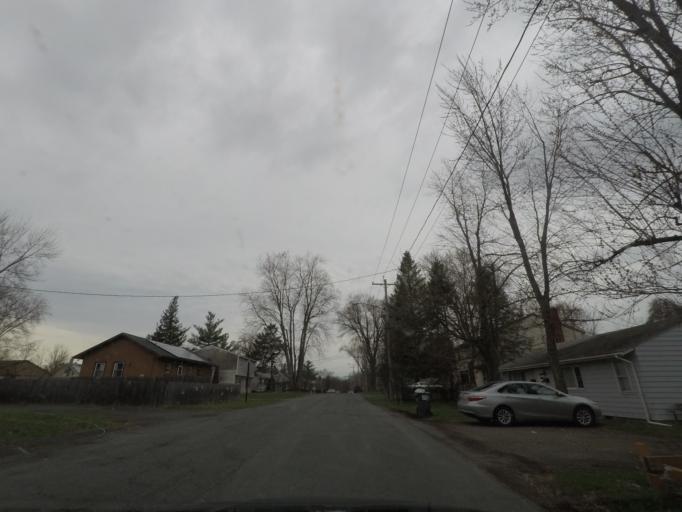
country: US
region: New York
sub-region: Rensselaer County
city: Hampton Manor
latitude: 42.6213
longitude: -73.7281
